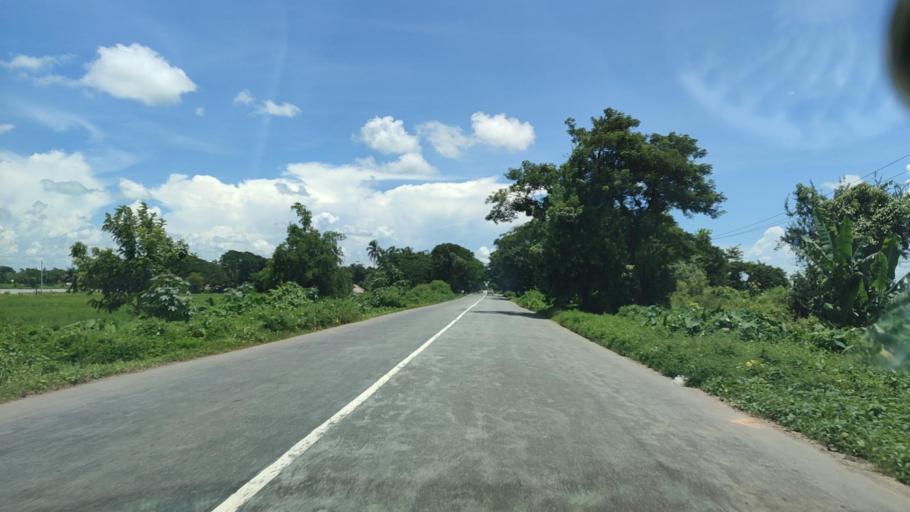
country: MM
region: Bago
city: Pyu
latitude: 18.3211
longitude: 96.5004
